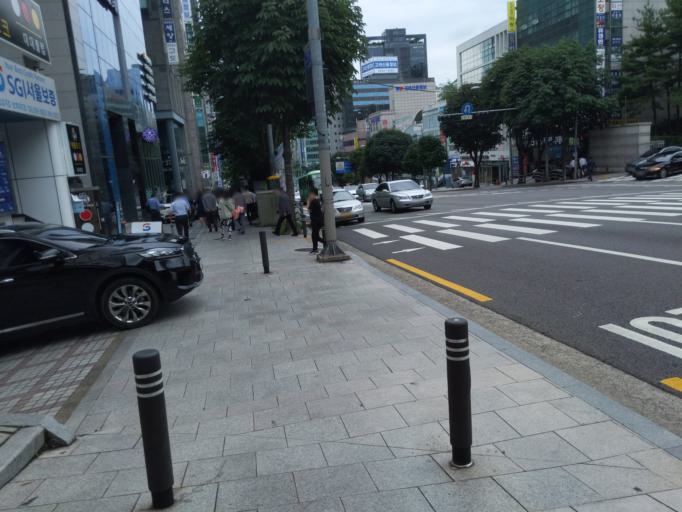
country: KR
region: Seoul
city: Seoul
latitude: 37.4960
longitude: 127.0133
